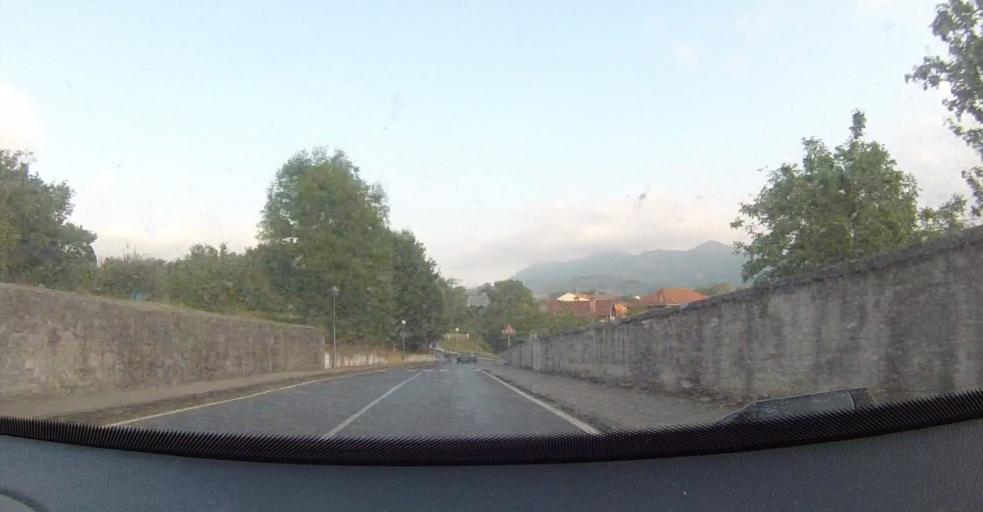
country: ES
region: Basque Country
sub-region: Bizkaia
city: Sopuerta
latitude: 43.2771
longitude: -3.1588
